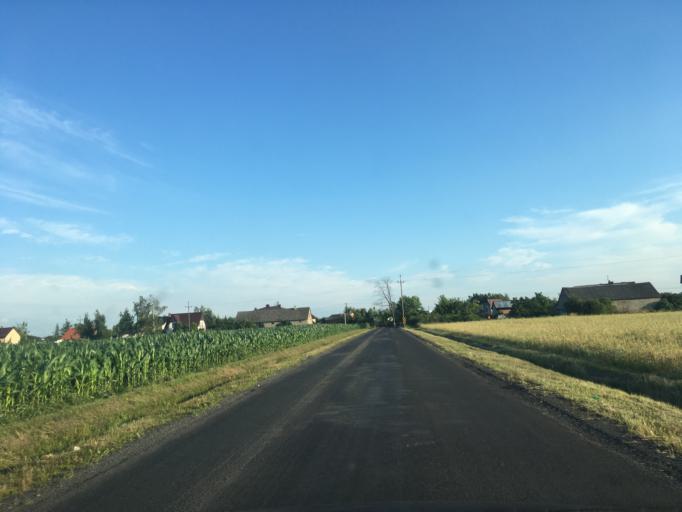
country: PL
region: Masovian Voivodeship
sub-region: Powiat grodziski
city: Grodzisk Mazowiecki
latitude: 52.1194
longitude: 20.5809
